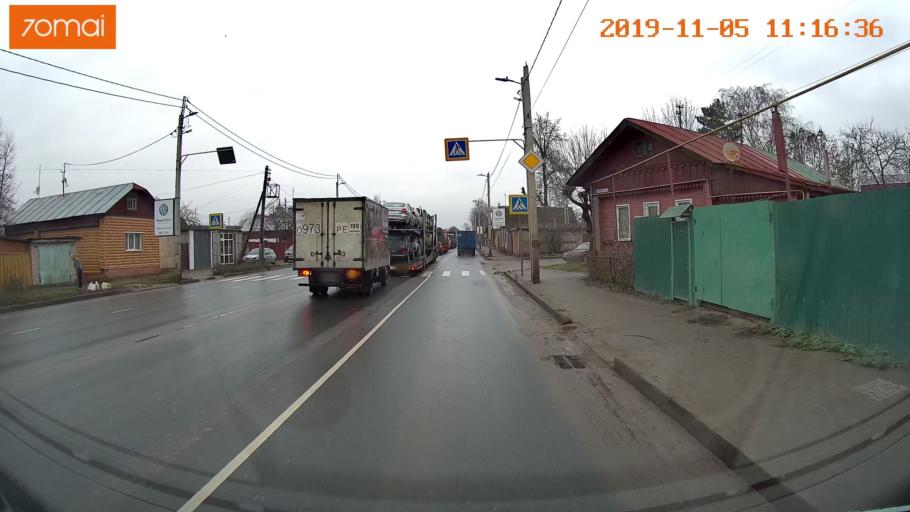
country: RU
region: Ivanovo
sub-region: Gorod Ivanovo
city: Ivanovo
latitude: 56.9862
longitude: 40.9533
